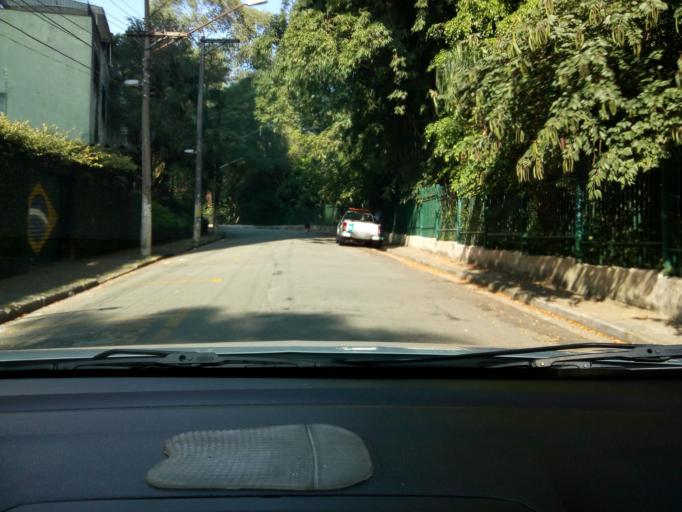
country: BR
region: Sao Paulo
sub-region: Sao Paulo
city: Sao Paulo
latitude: -23.5750
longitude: -46.6271
